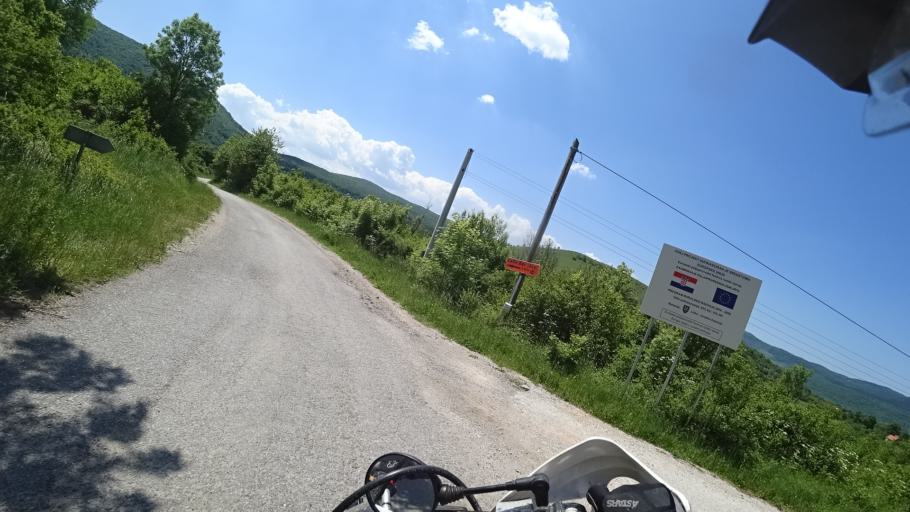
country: HR
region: Karlovacka
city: Plaski
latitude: 44.9578
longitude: 15.3432
